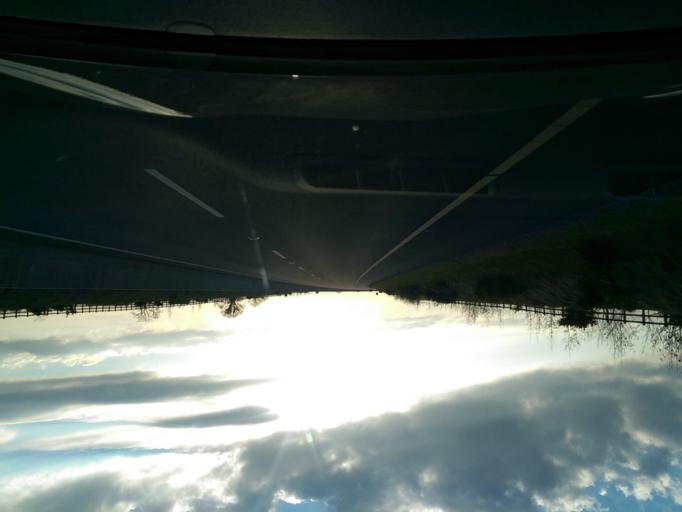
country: IE
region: Munster
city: Nenagh Bridge
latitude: 52.8736
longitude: -8.0432
